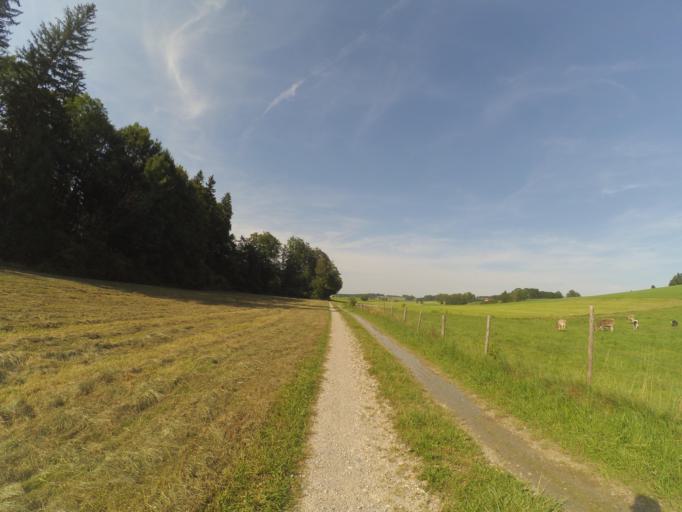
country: DE
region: Bavaria
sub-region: Swabia
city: Unteregg
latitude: 47.9712
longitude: 10.4598
